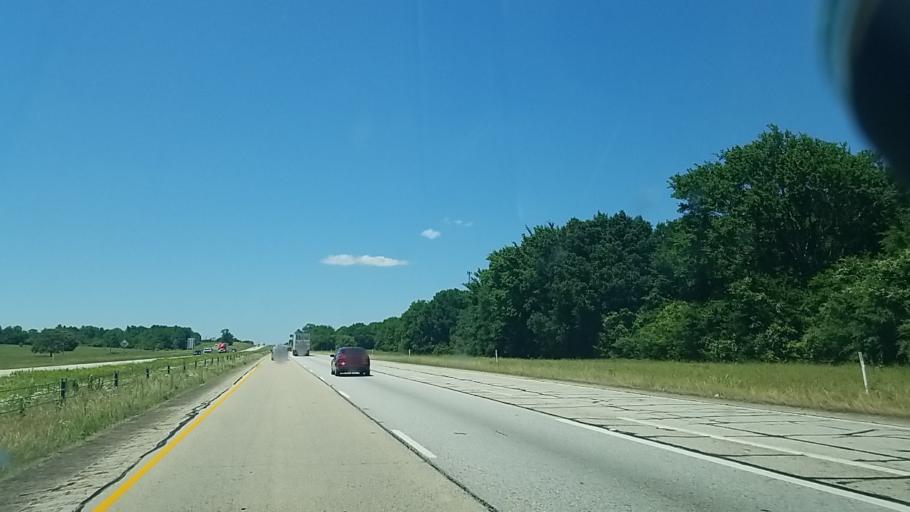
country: US
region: Texas
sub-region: Leon County
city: Centerville
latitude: 31.1532
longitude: -95.9838
